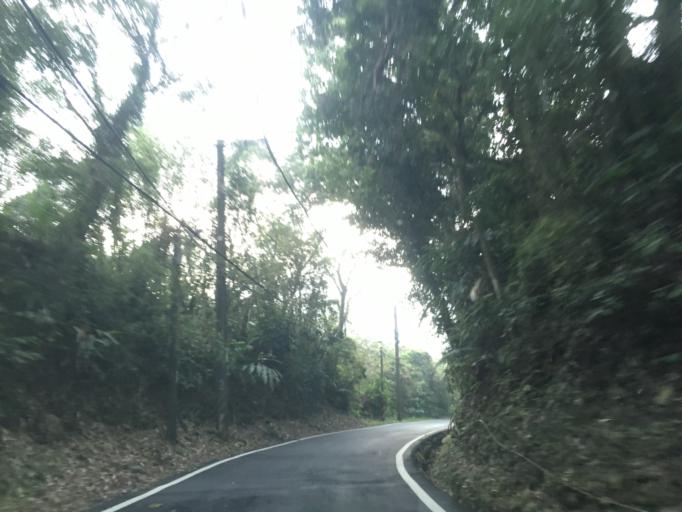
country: TW
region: Taiwan
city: Daxi
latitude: 24.8817
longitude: 121.3053
